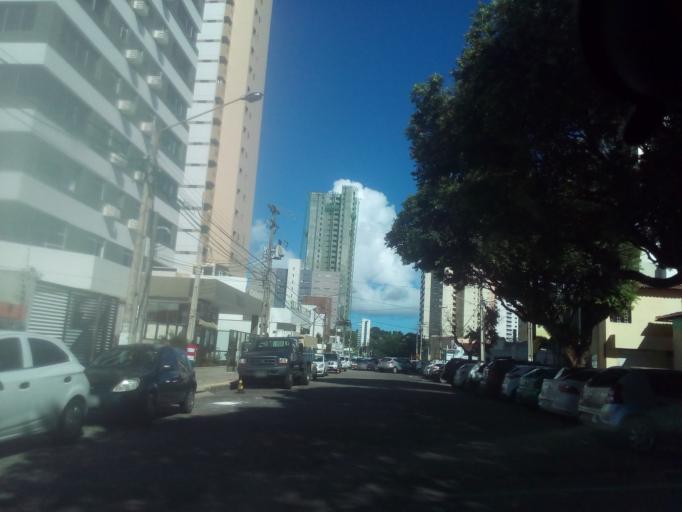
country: BR
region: Rio Grande do Norte
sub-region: Natal
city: Natal
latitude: -5.7878
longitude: -35.2031
